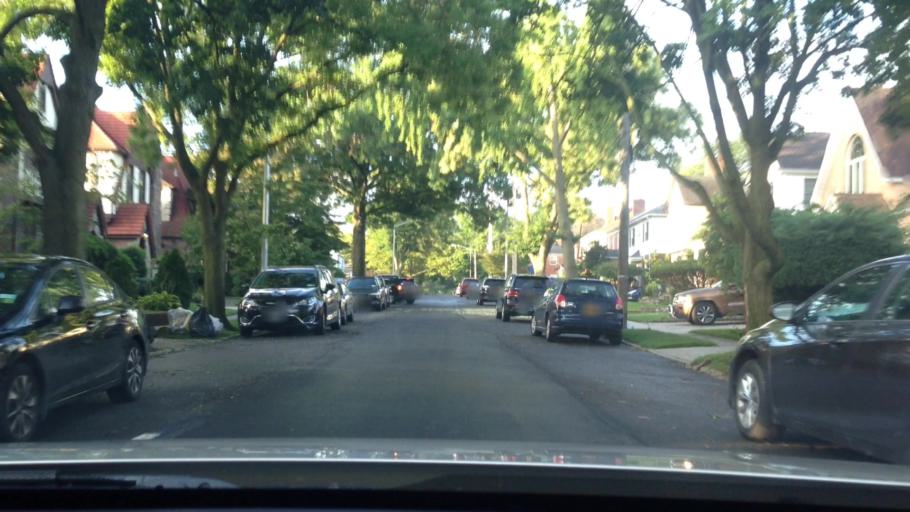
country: US
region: New York
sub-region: Nassau County
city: East Atlantic Beach
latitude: 40.7704
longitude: -73.7941
